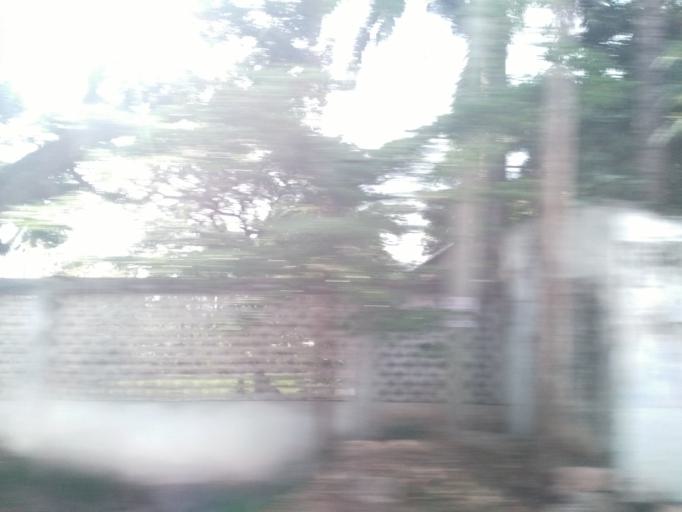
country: TZ
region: Dar es Salaam
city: Dar es Salaam
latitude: -6.8116
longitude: 39.2777
